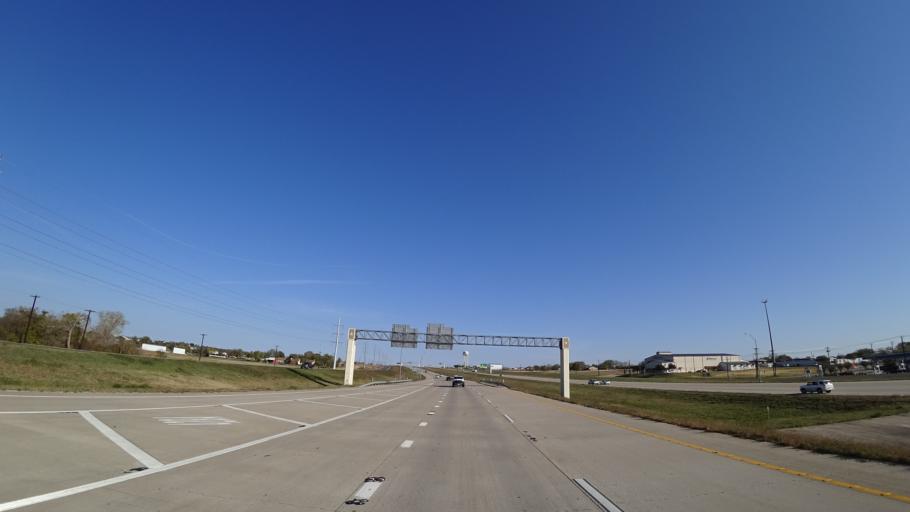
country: US
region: Texas
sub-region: Travis County
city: Pflugerville
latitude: 30.4842
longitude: -97.5856
